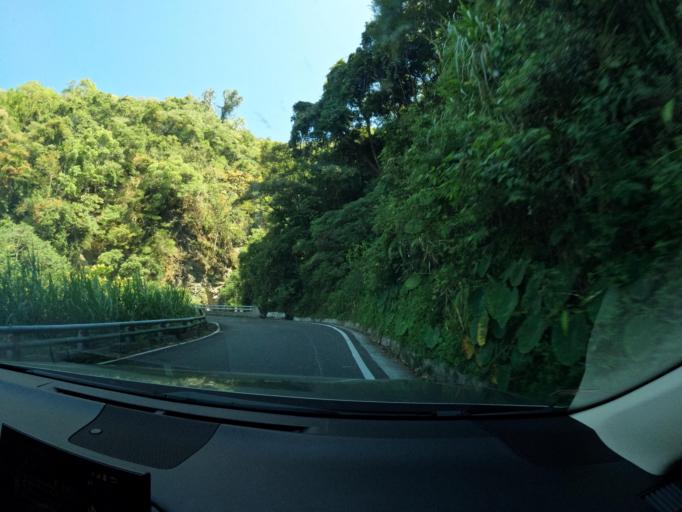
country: TW
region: Taiwan
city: Yujing
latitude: 23.2679
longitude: 120.8492
